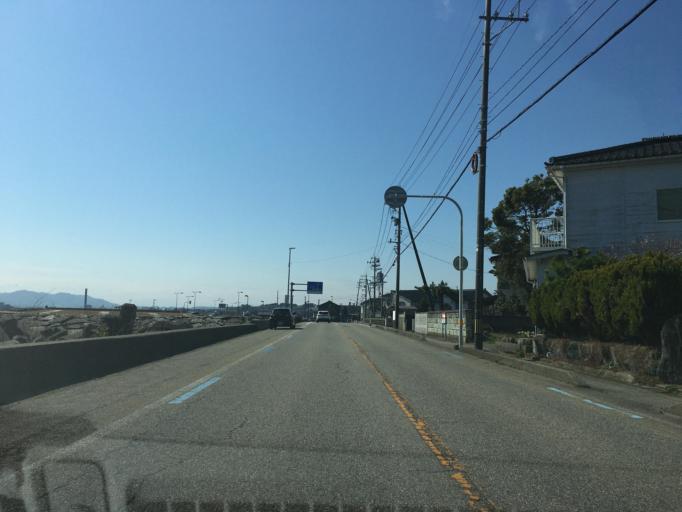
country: JP
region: Toyama
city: Himi
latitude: 36.8761
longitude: 136.9845
